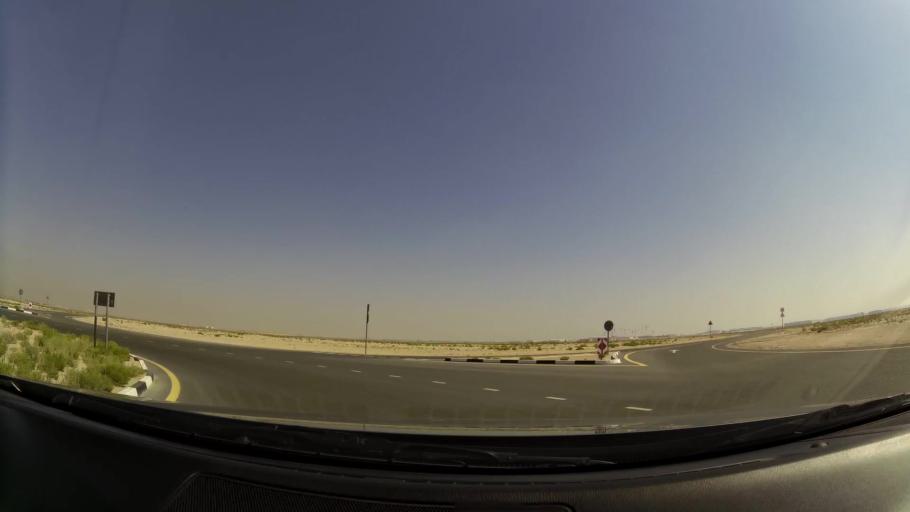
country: AE
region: Dubai
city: Dubai
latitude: 24.8999
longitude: 55.0538
